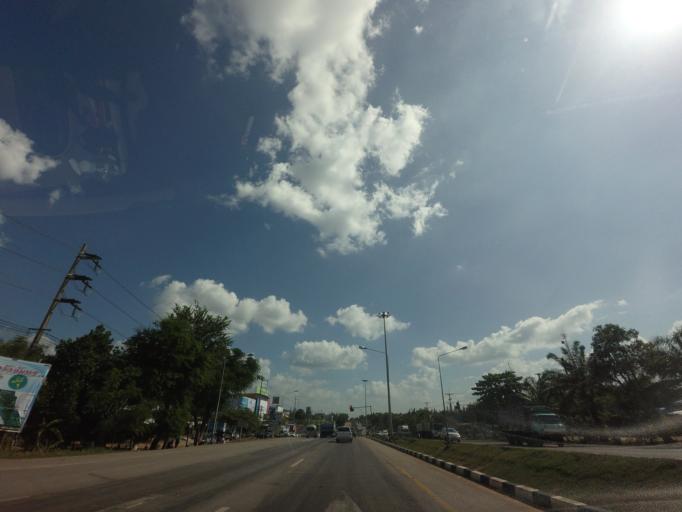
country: TH
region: Rayong
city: Wang Chan
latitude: 12.9375
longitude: 101.5216
